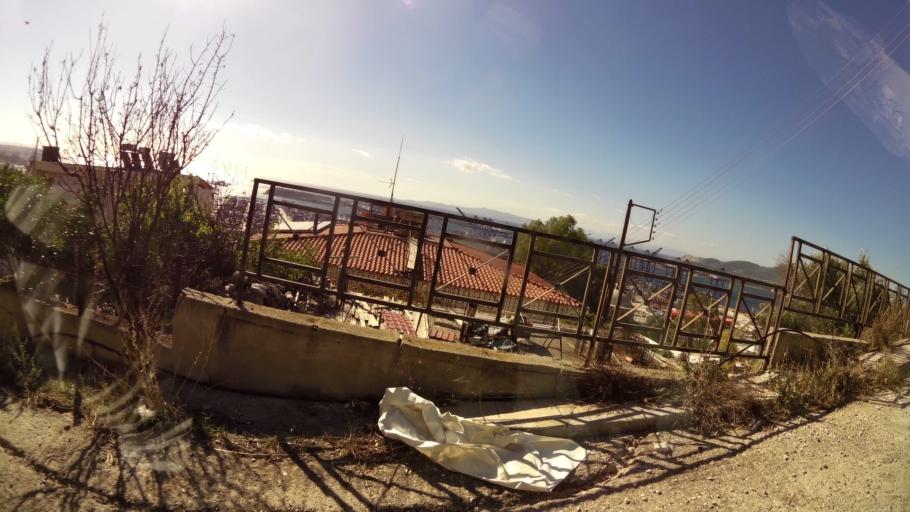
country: GR
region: Attica
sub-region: Nomos Piraios
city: Perama
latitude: 37.9654
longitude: 23.5899
